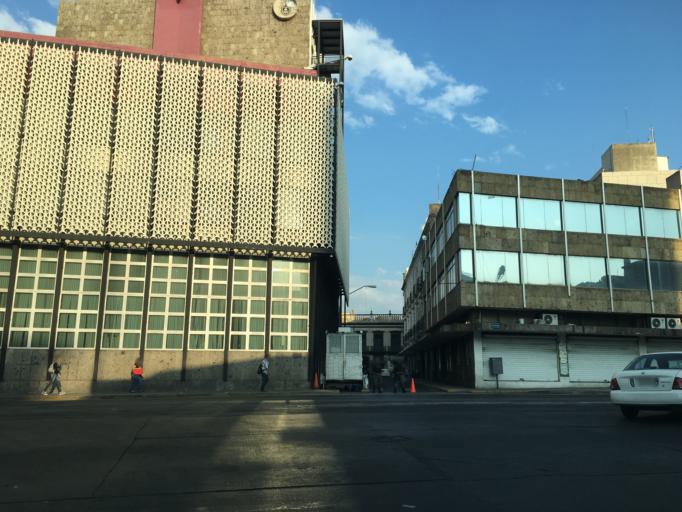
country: MX
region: Jalisco
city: Guadalajara
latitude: 20.6711
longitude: -103.3471
